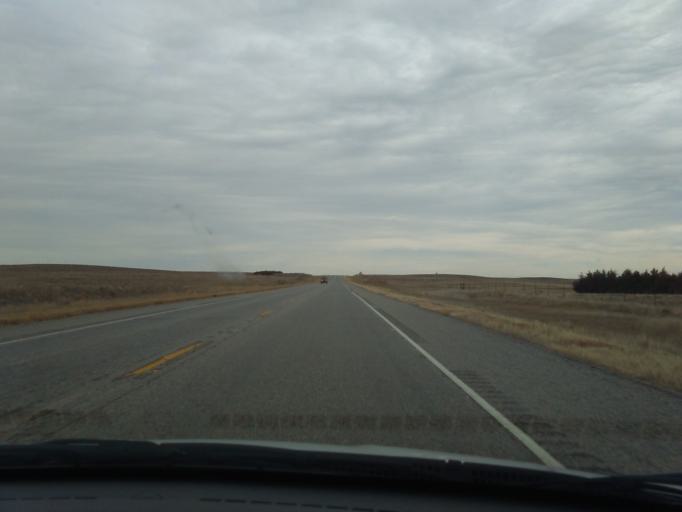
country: US
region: Colorado
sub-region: Washington County
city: Akron
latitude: 40.2234
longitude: -103.3873
